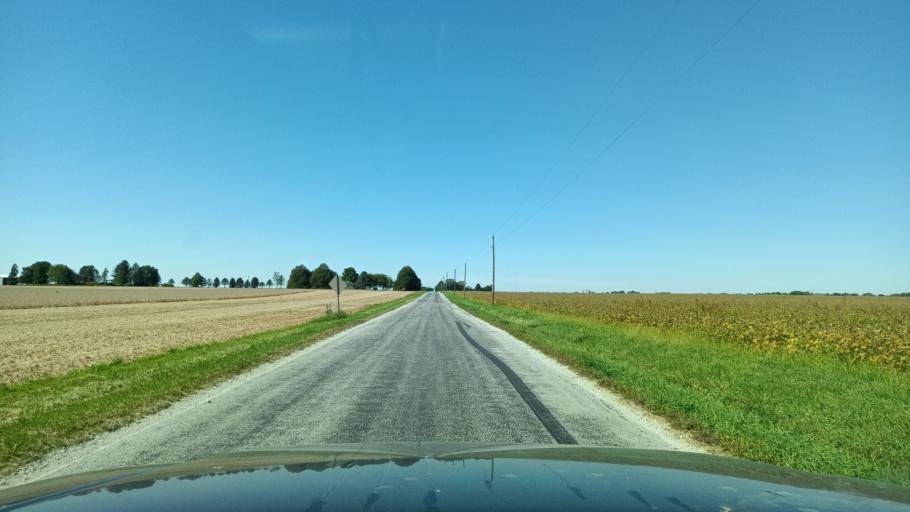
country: US
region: Illinois
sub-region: Champaign County
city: Mahomet
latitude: 40.0987
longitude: -88.3707
